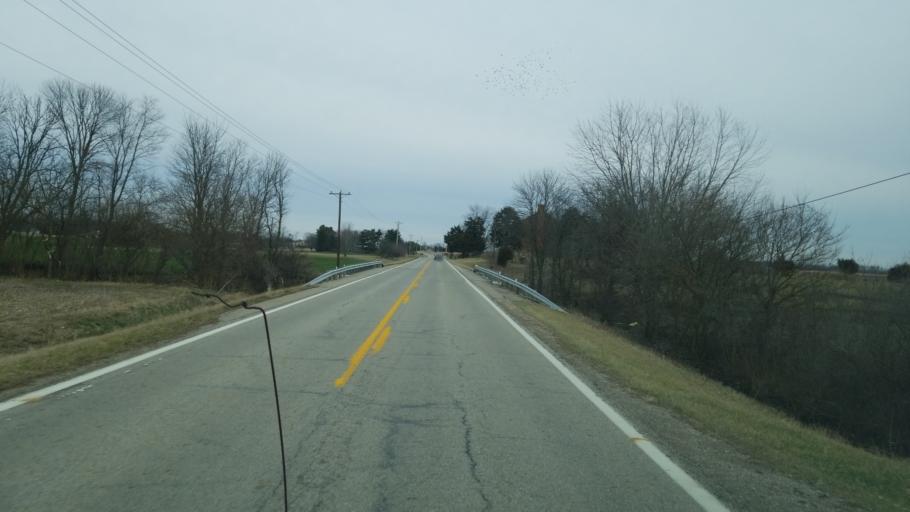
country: US
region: Ohio
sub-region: Pickaway County
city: Williamsport
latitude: 39.5668
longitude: -83.0704
